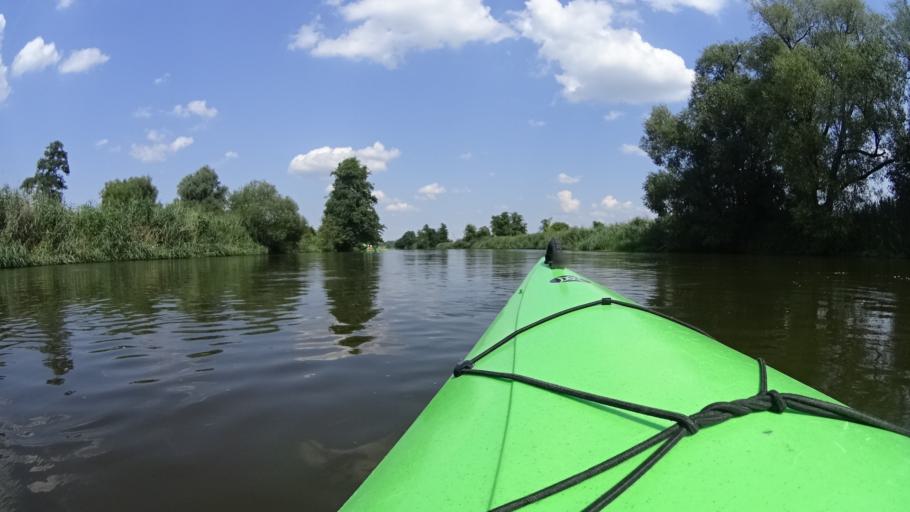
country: PL
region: Masovian Voivodeship
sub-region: Powiat bialobrzeski
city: Wysmierzyce
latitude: 51.6485
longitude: 20.8171
